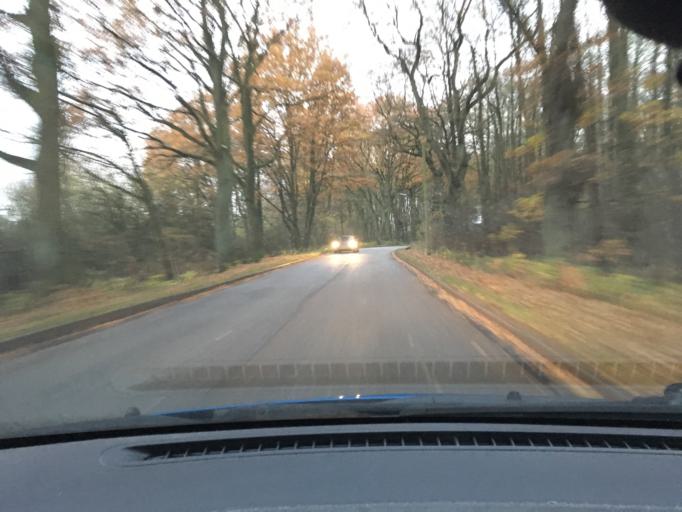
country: DE
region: Lower Saxony
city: Winsen
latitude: 53.4053
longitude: 10.2072
